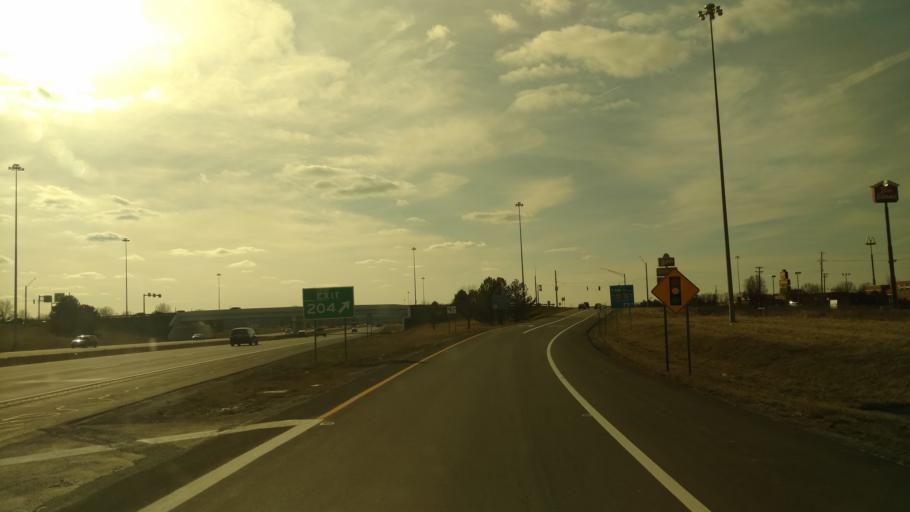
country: US
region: Ohio
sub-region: Medina County
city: Lodi
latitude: 40.9978
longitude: -81.9937
